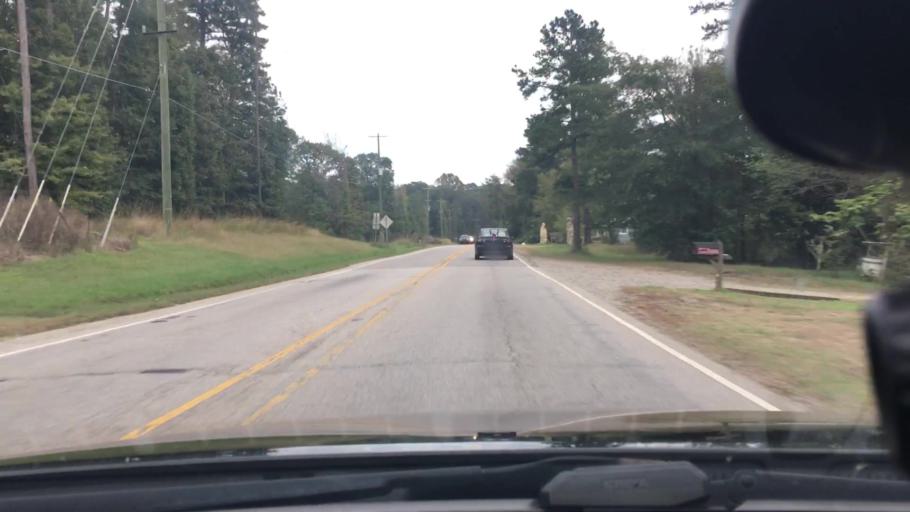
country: US
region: North Carolina
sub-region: Moore County
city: Robbins
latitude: 35.4042
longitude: -79.5729
